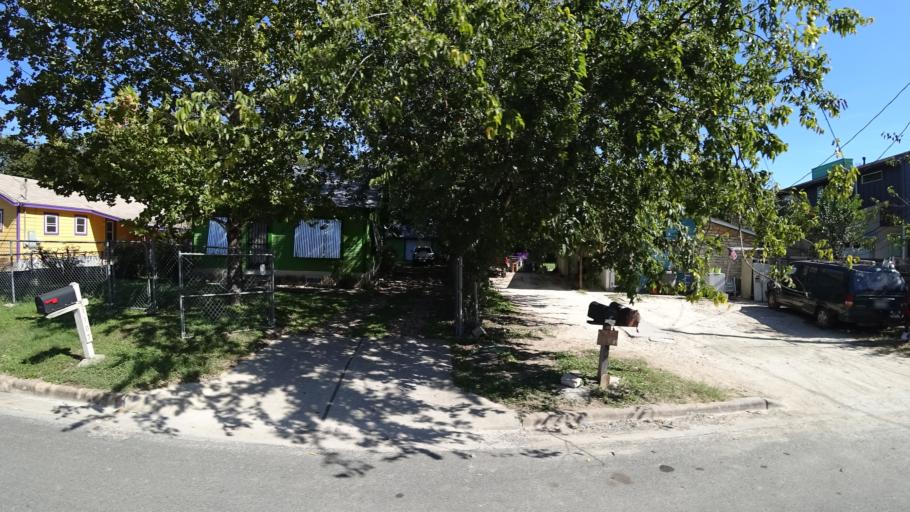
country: US
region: Texas
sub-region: Travis County
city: Austin
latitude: 30.2691
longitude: -97.6879
